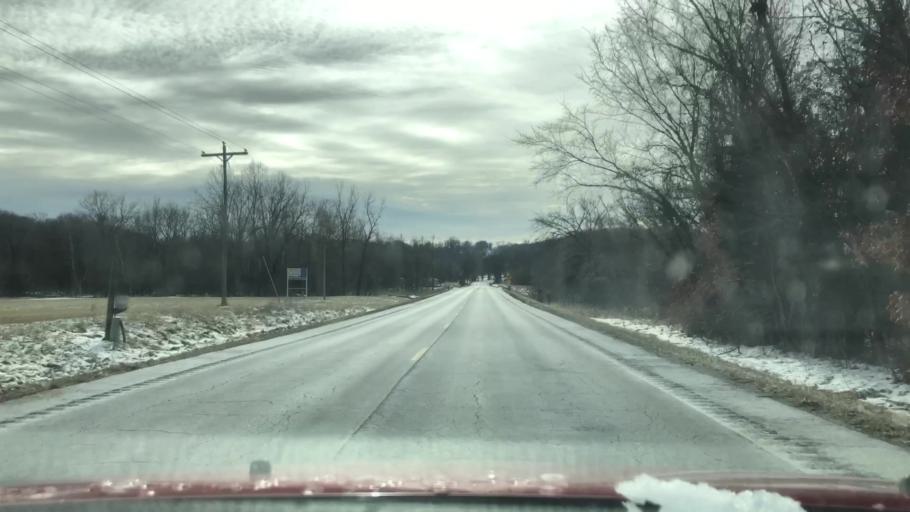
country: US
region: Missouri
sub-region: Jackson County
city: Oak Grove
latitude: 38.9455
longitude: -94.1319
